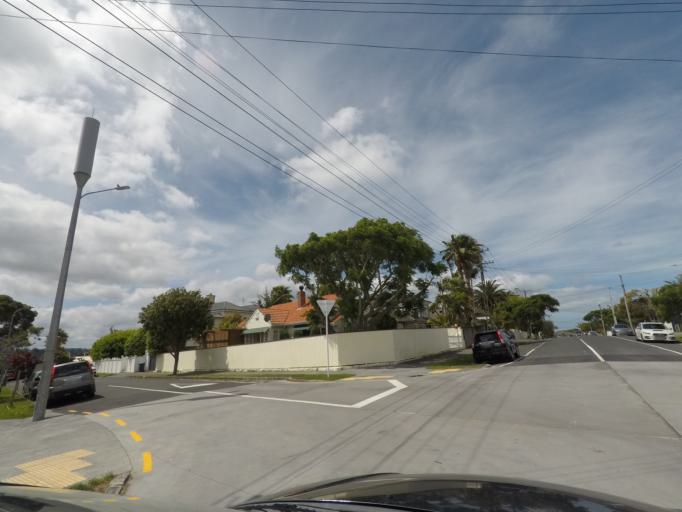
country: NZ
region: Auckland
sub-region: Auckland
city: Auckland
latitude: -36.8436
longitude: 174.7312
